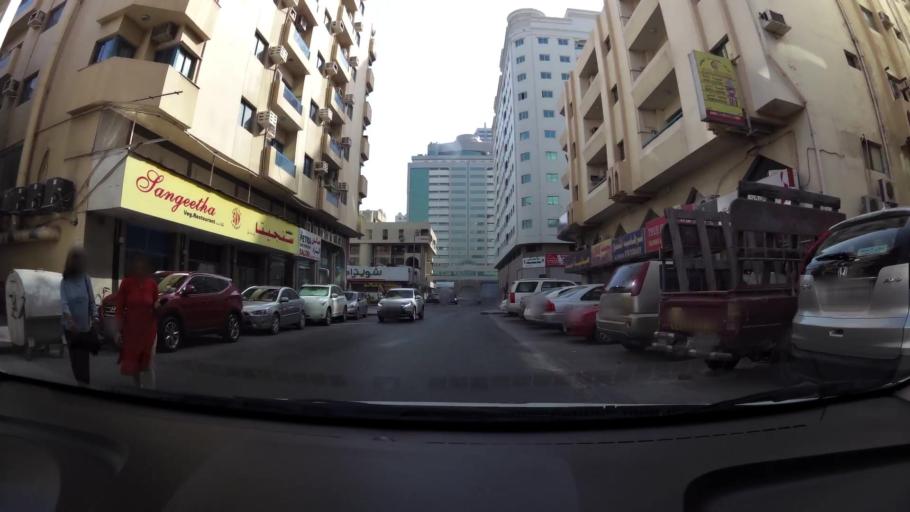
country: AE
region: Ash Shariqah
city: Sharjah
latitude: 25.3361
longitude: 55.3923
